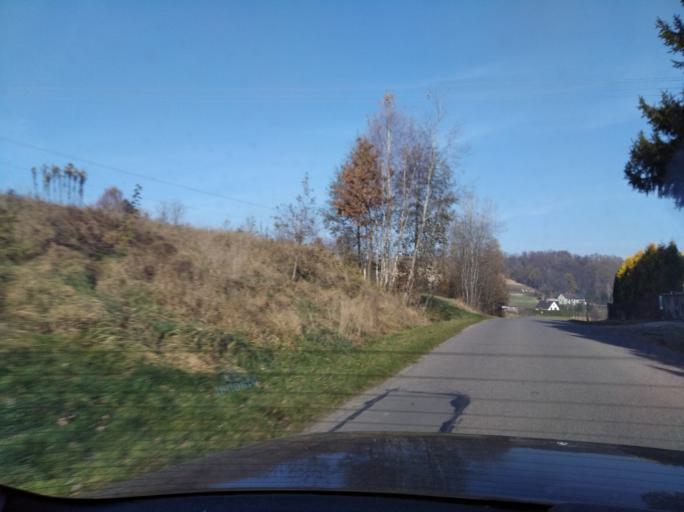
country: PL
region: Subcarpathian Voivodeship
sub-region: Powiat ropczycko-sedziszowski
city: Wielopole Skrzynskie
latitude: 49.9408
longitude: 21.5786
